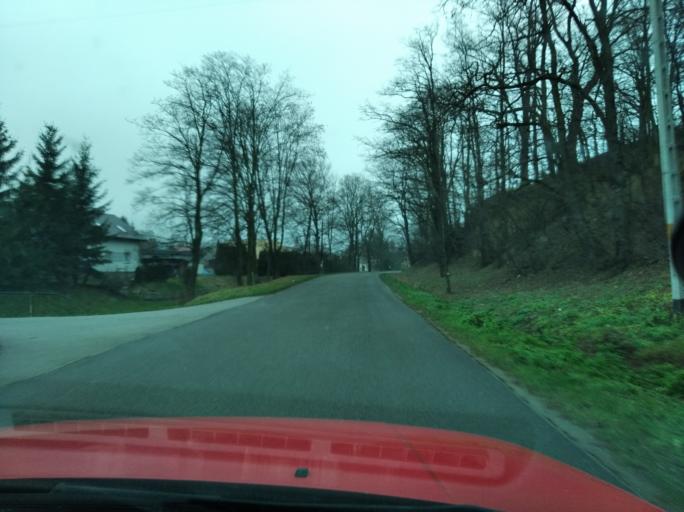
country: PL
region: Subcarpathian Voivodeship
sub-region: Powiat przeworski
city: Rozborz
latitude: 50.0555
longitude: 22.5461
